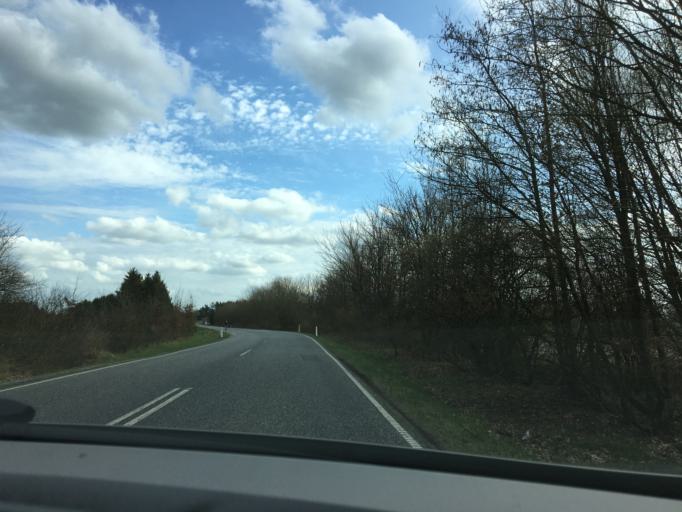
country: DK
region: South Denmark
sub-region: Vejle Kommune
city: Jelling
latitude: 55.8074
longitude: 9.3594
